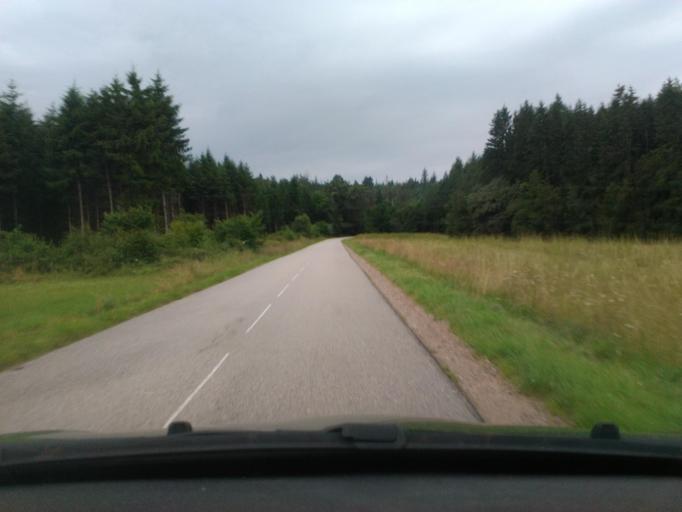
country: FR
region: Lorraine
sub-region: Departement des Vosges
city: Bruyeres
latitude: 48.2124
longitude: 6.7500
